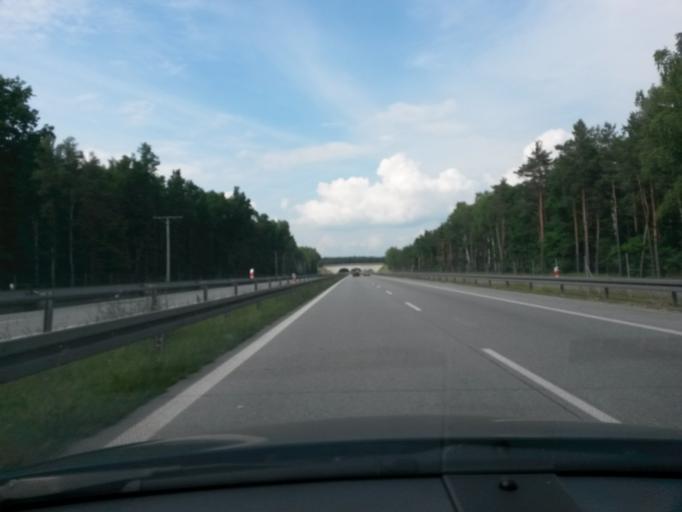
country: PL
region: Lodz Voivodeship
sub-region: Powiat tomaszowski
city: Lubochnia
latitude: 51.5729
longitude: 20.0268
